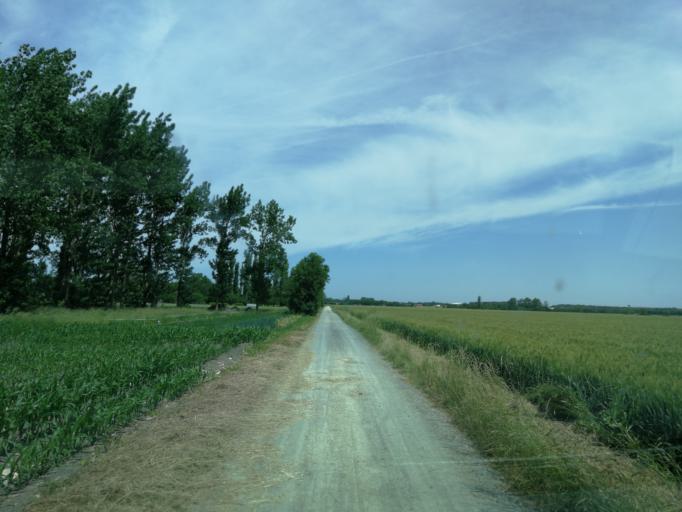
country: FR
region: Pays de la Loire
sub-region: Departement de la Vendee
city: Le Langon
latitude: 46.3735
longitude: -0.9536
